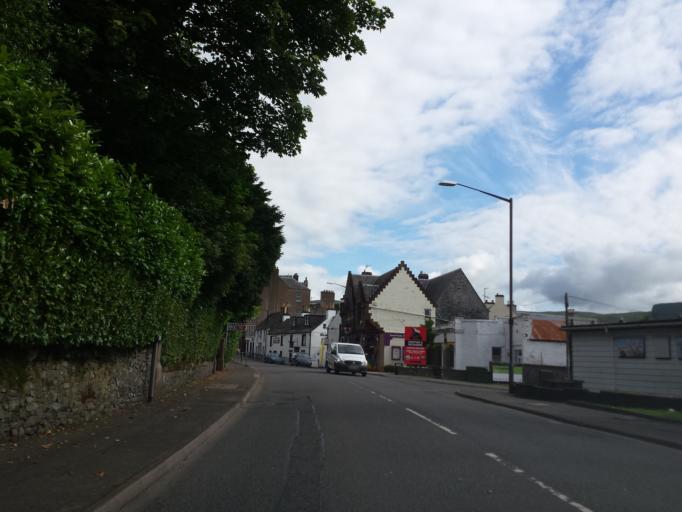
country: GB
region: Scotland
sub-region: Dumfries and Galloway
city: Moffat
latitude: 55.3310
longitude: -3.4442
